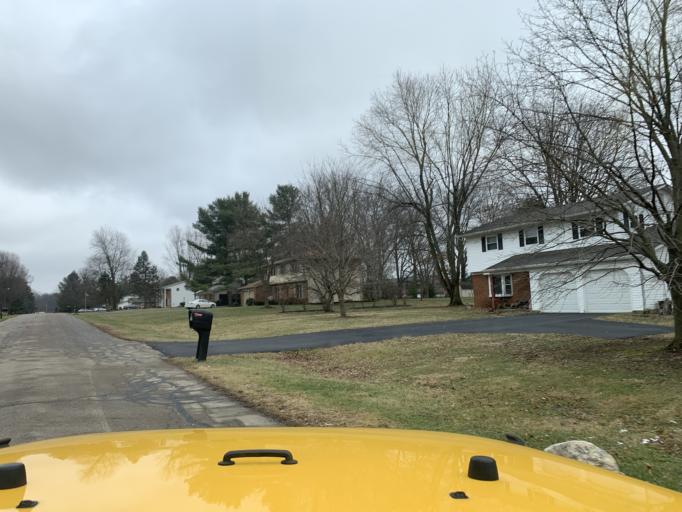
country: US
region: Ohio
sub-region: Franklin County
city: New Albany
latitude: 40.0935
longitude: -82.8089
